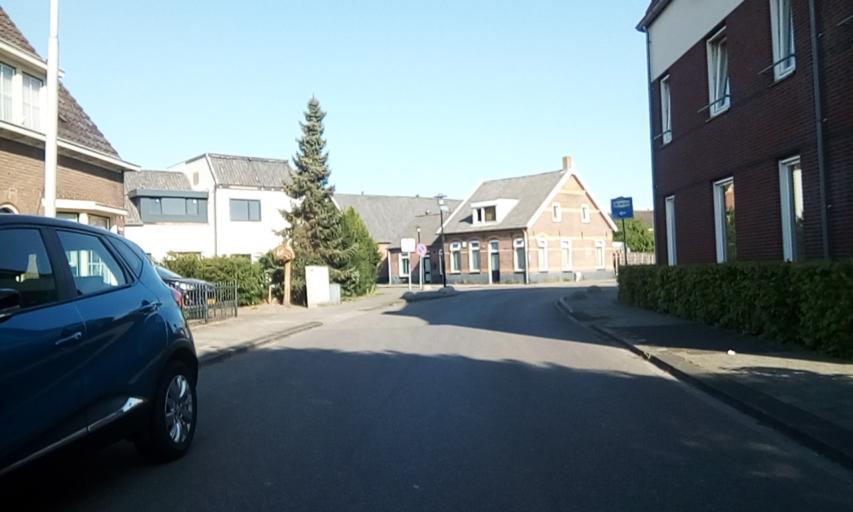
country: NL
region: Gelderland
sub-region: Gemeente Druten
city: Druten
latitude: 51.8914
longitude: 5.6138
